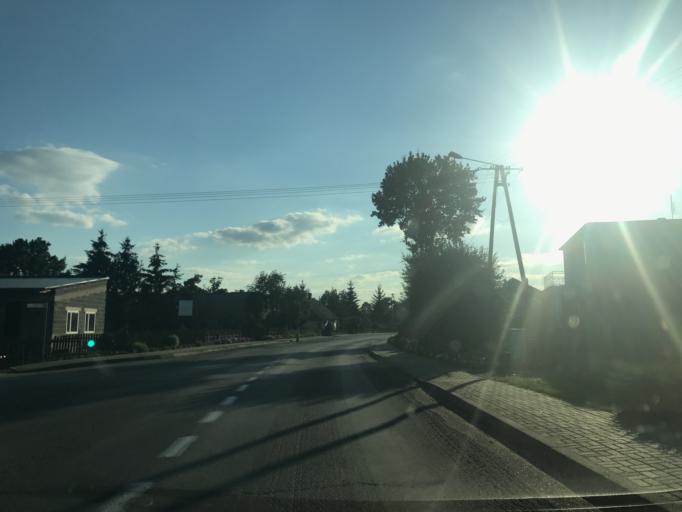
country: PL
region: Greater Poland Voivodeship
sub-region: Powiat pleszewski
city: Gizalki
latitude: 52.0456
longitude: 17.8173
